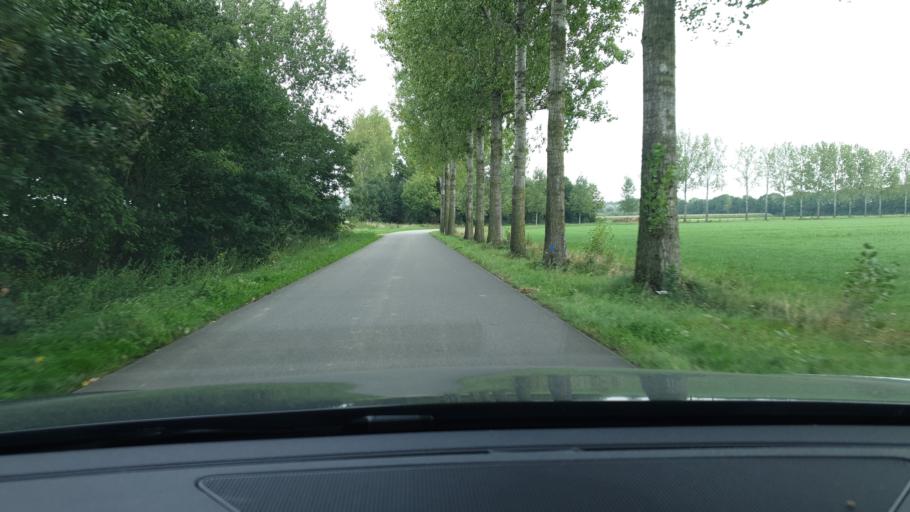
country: NL
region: Gelderland
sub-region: Gemeente Wijchen
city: Bergharen
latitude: 51.8375
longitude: 5.6356
